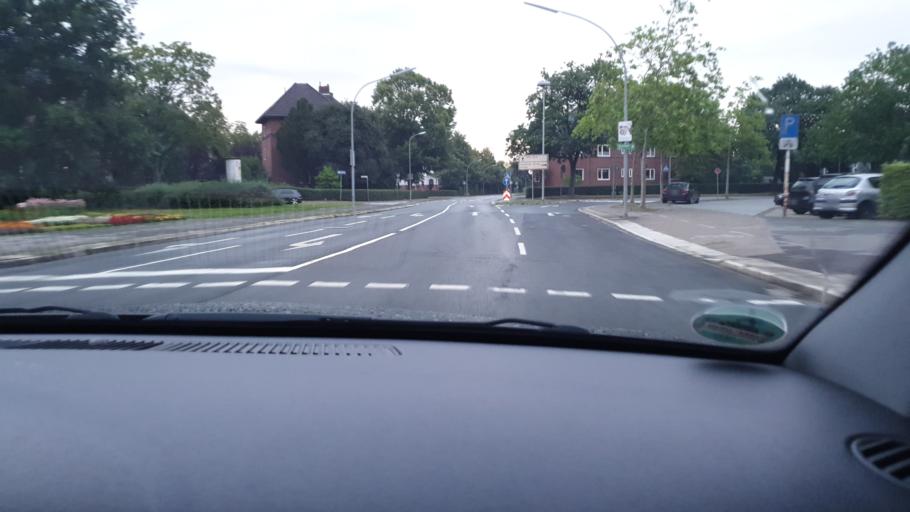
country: DE
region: Lower Saxony
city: Wilhelmshaven
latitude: 53.5283
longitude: 8.1133
